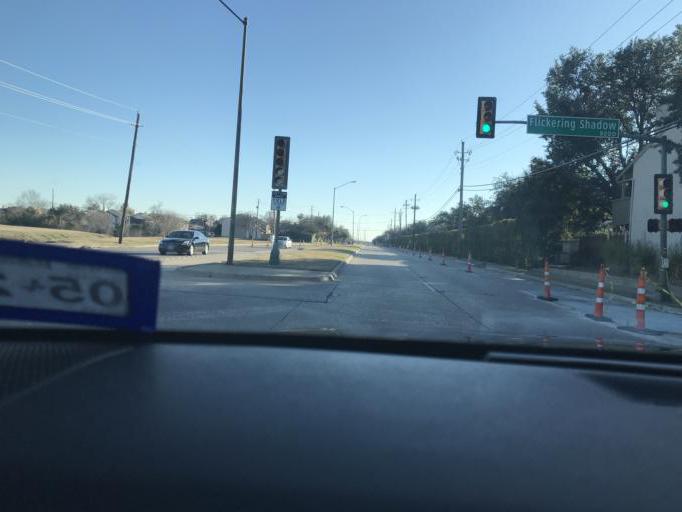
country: US
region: Texas
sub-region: Dallas County
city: Richardson
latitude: 32.9209
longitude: -96.7355
